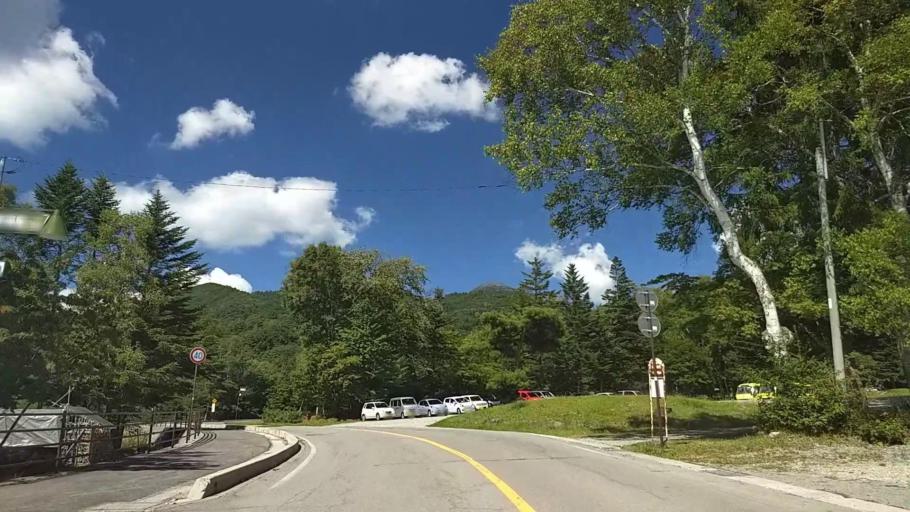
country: JP
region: Nagano
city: Chino
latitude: 36.0585
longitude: 138.2676
